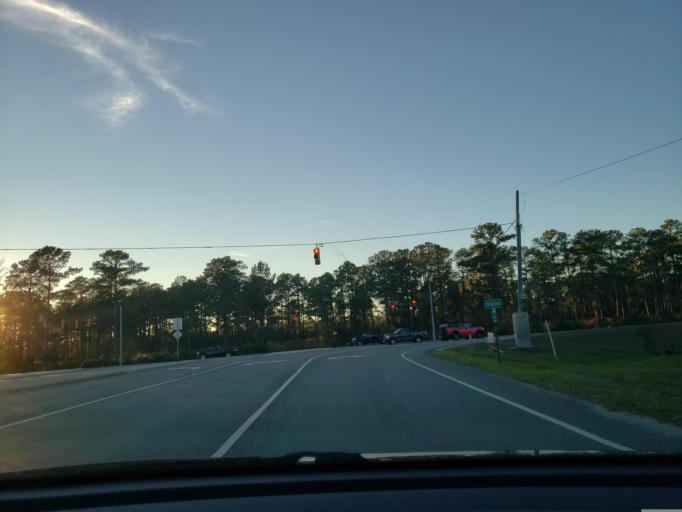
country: US
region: North Carolina
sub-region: Onslow County
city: Sneads Ferry
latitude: 34.5892
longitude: -77.4792
